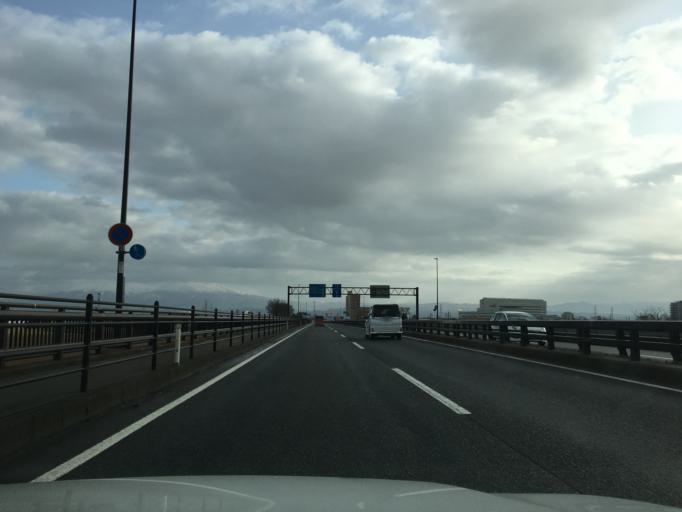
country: JP
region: Yamagata
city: Sakata
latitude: 38.8878
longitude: 139.8443
